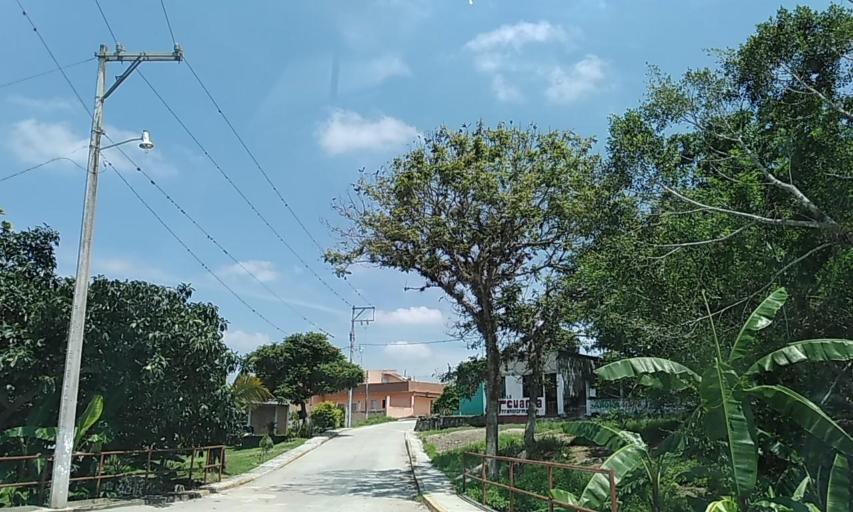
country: MX
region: Veracruz
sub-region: Emiliano Zapata
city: Dos Rios
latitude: 19.4405
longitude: -96.7540
